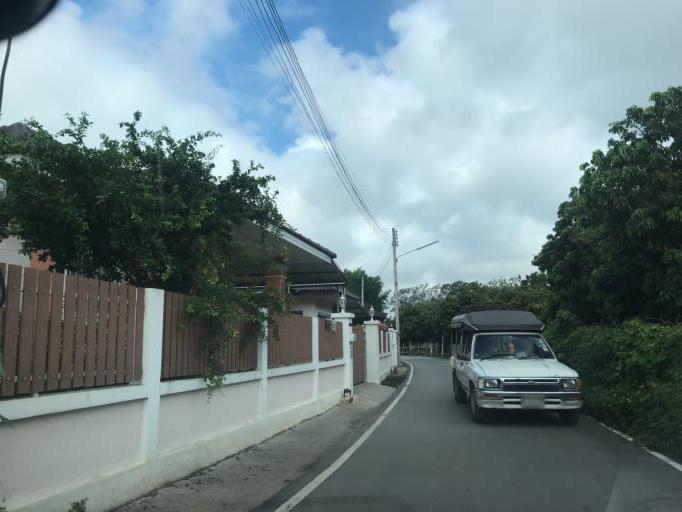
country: TH
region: Chiang Mai
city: Saraphi
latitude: 18.7421
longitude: 99.0180
